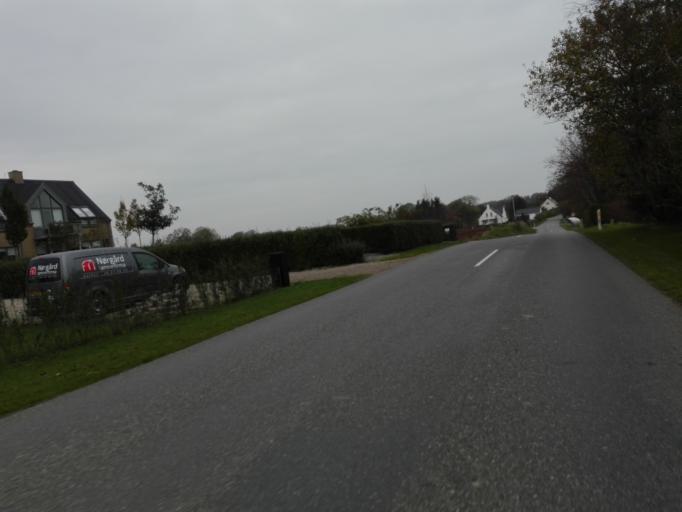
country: DK
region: Central Jutland
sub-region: Arhus Kommune
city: Beder
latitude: 56.0465
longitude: 10.2410
